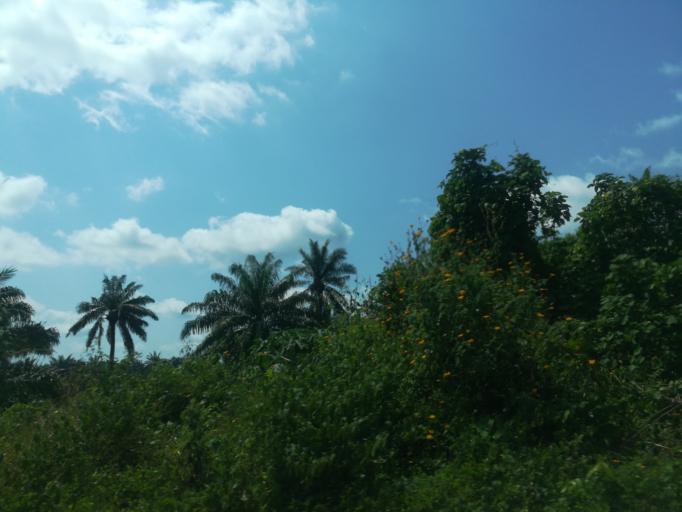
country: NG
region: Oyo
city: Moniya
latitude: 7.5819
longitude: 3.9112
